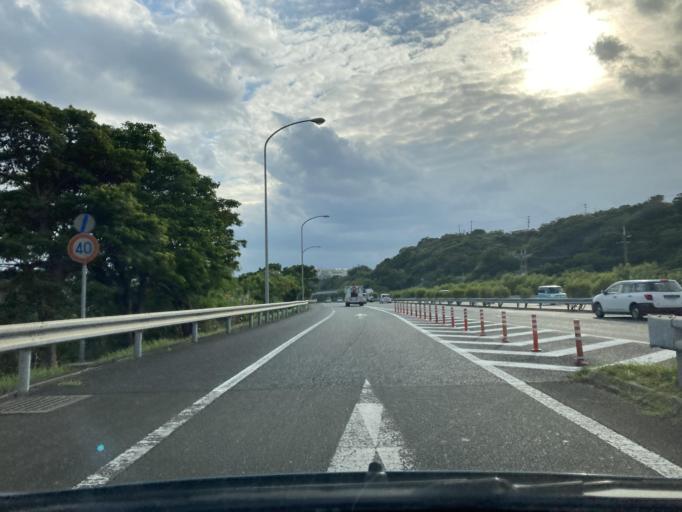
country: JP
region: Okinawa
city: Ginowan
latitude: 26.2741
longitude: 127.7794
